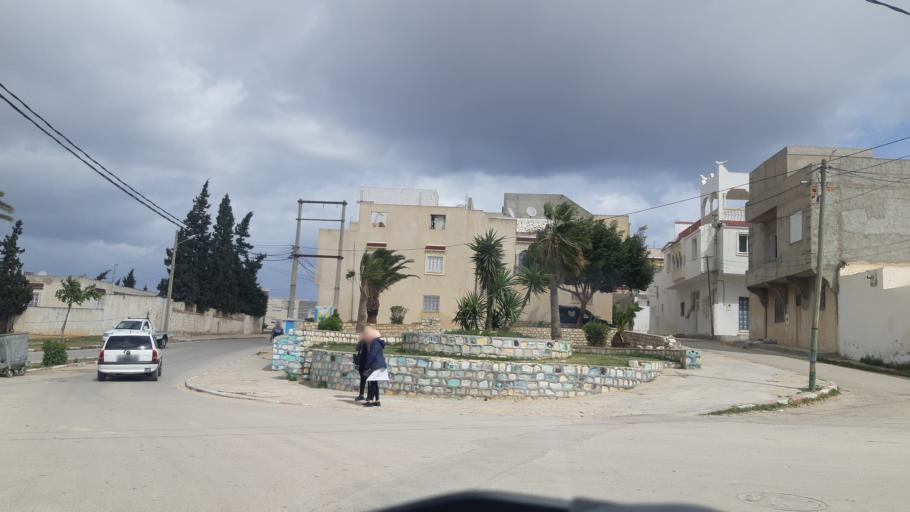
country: TN
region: Susah
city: Akouda
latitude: 35.8624
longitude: 10.5397
